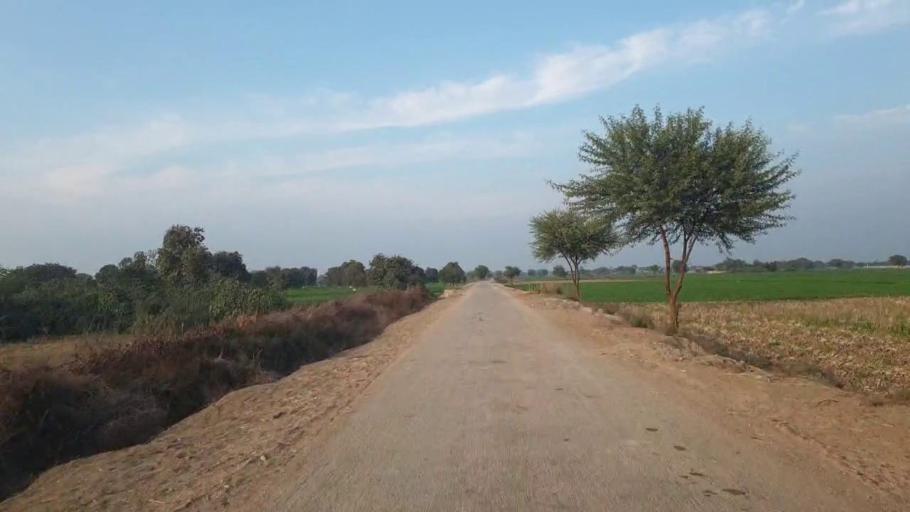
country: PK
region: Sindh
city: Shahpur Chakar
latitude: 26.1118
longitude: 68.5465
